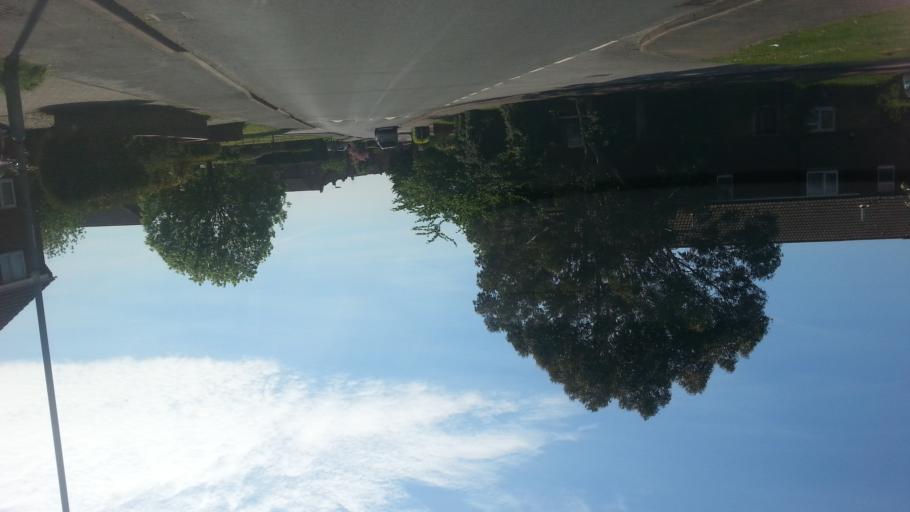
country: GB
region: England
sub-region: Cambridgeshire
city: Warboys
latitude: 52.4063
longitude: -0.0817
